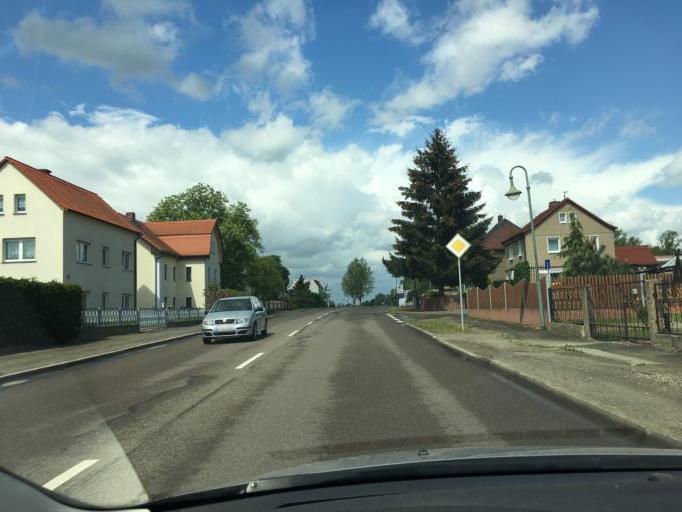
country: DE
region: Saxony
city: Borna
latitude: 51.1066
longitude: 12.5124
